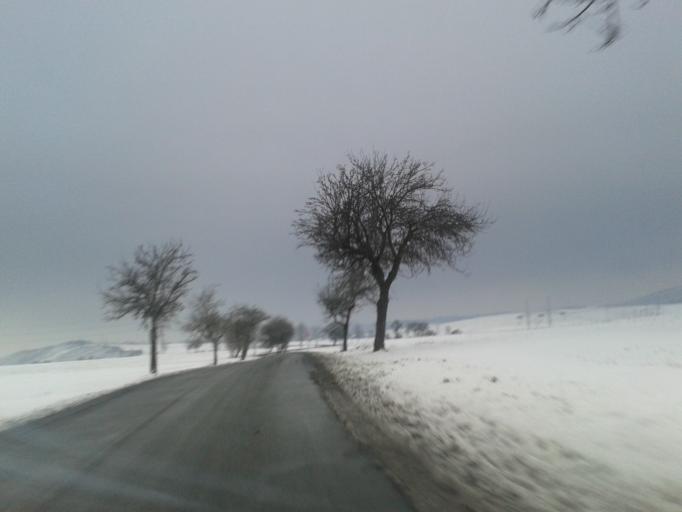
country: CZ
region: Central Bohemia
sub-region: Okres Beroun
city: Beroun
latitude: 49.9267
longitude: 14.0835
